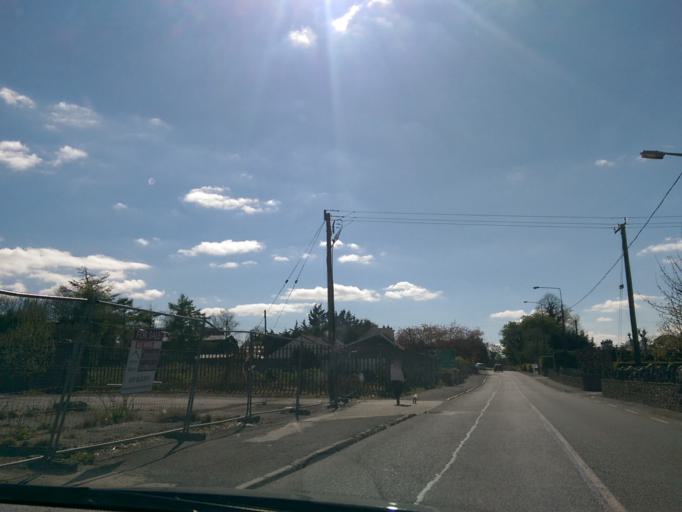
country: IE
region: Leinster
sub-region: Laois
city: Stradbally
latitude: 53.0127
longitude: -7.1392
